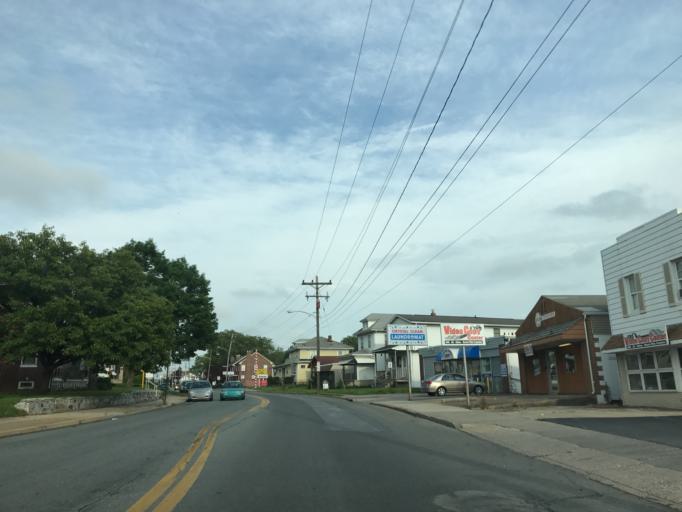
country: US
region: Pennsylvania
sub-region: York County
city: Valley View
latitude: 39.9596
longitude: -76.7023
